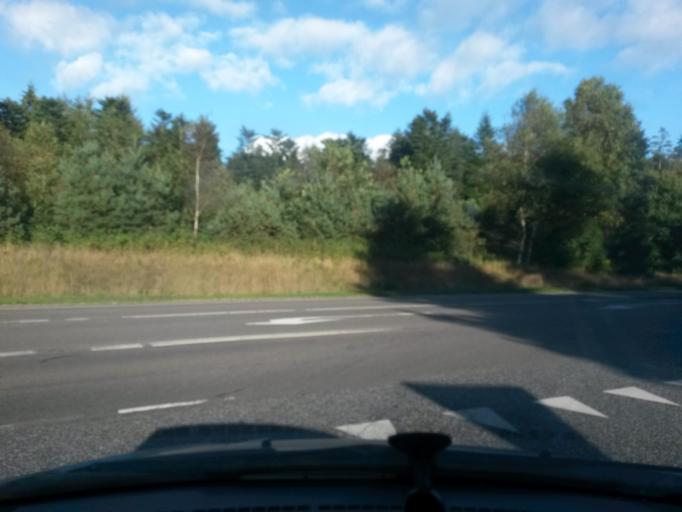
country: DK
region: Central Jutland
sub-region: Viborg Kommune
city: Karup
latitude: 56.3089
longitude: 9.2779
